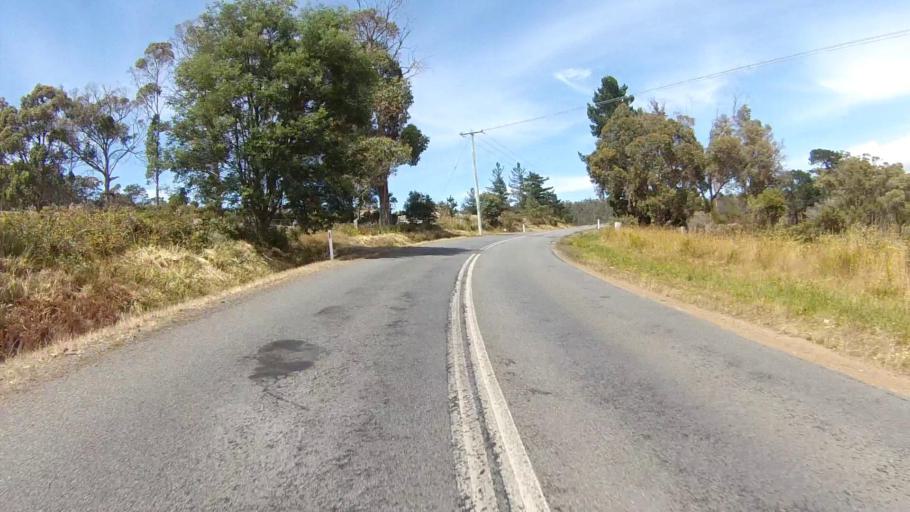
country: AU
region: Tasmania
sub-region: Huon Valley
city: Cygnet
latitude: -43.2176
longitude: 147.1225
